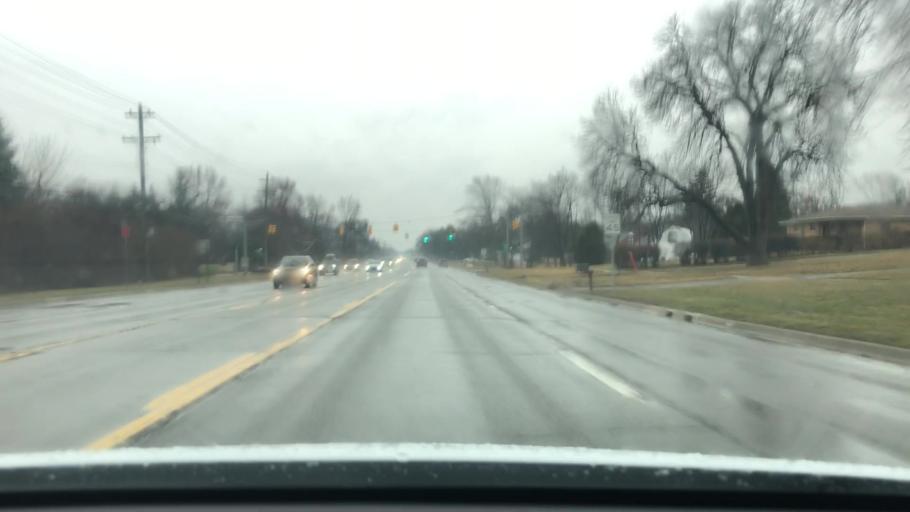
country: US
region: Michigan
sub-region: Oakland County
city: Troy
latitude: 42.5718
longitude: -83.1678
